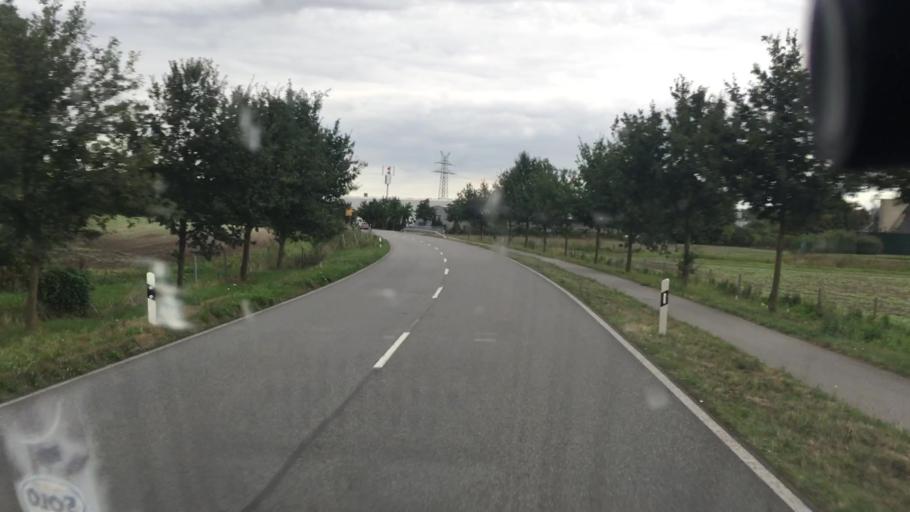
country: DE
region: Lower Saxony
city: Lohne
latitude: 52.6543
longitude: 8.2010
